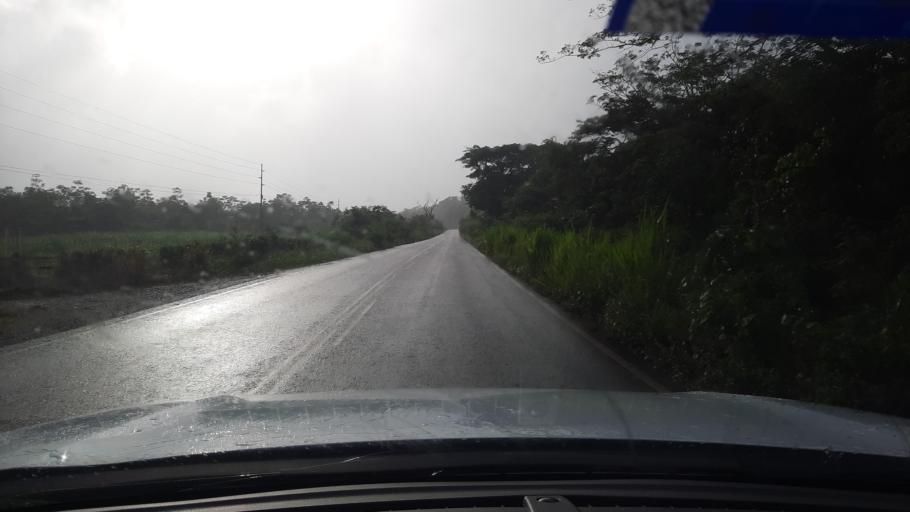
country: CR
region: Guanacaste
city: La Cruz
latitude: 11.0461
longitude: -85.4837
